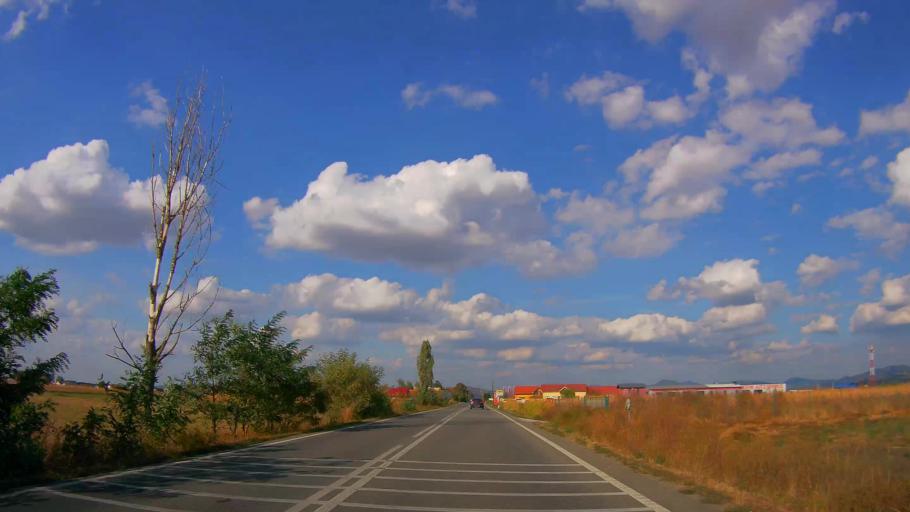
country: RO
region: Satu Mare
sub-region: Comuna Turulung
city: Turulung
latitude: 47.9223
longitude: 23.0837
